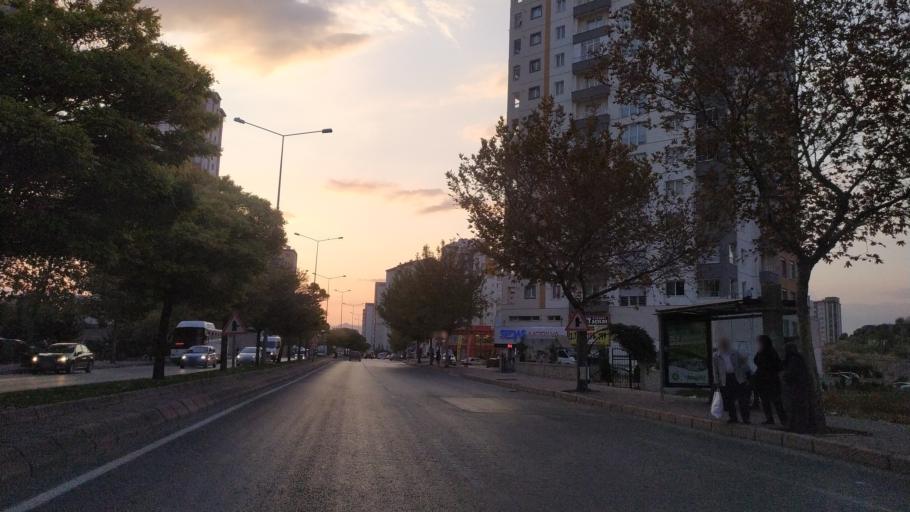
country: TR
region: Kayseri
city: Talas
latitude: 38.7084
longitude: 35.5584
